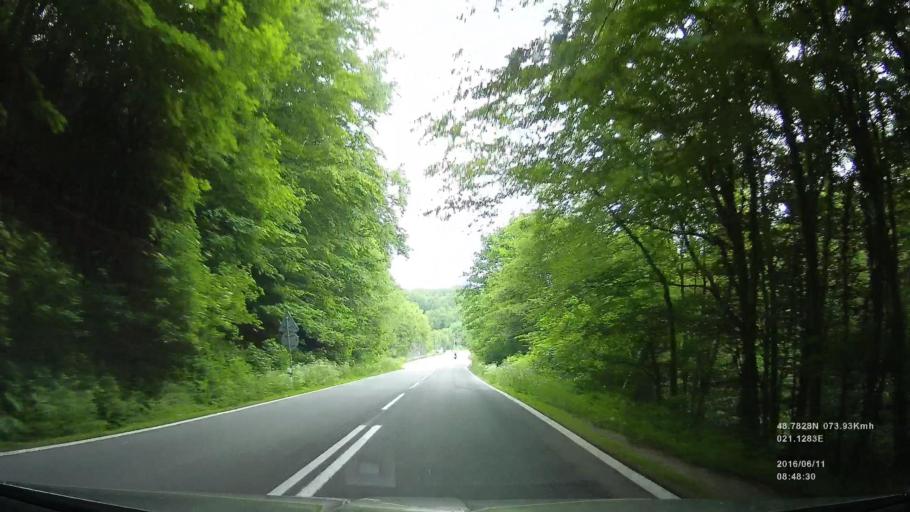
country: SK
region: Kosicky
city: Kosice
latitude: 48.7694
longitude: 21.1662
